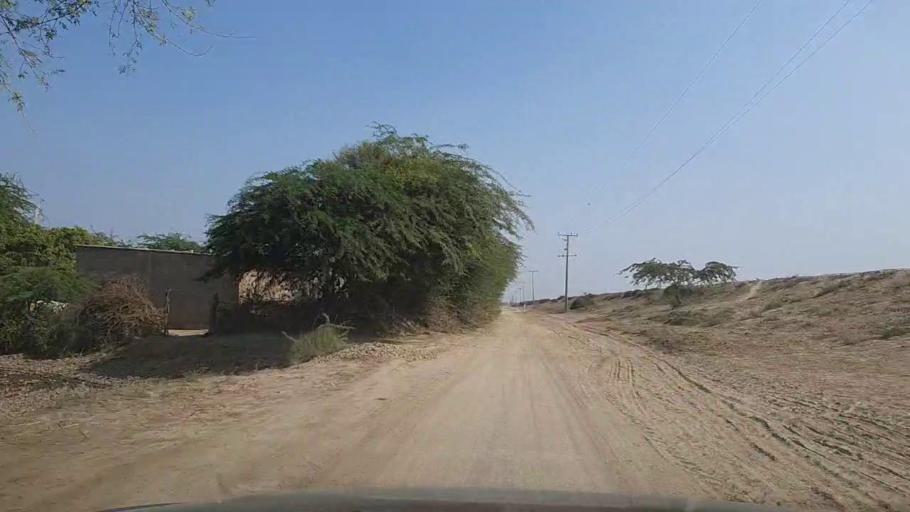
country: PK
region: Sindh
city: Thatta
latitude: 24.5885
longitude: 67.9329
